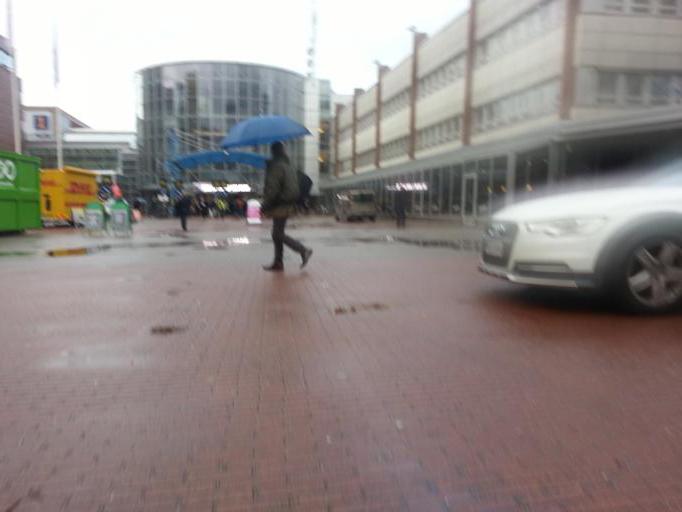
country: FI
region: Uusimaa
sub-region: Helsinki
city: Helsinki
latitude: 60.2016
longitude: 24.9364
